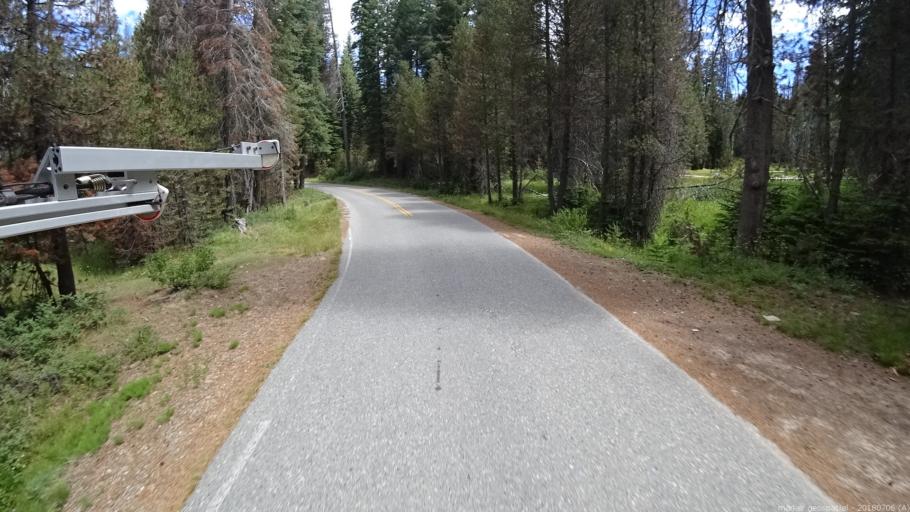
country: US
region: California
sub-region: Madera County
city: Oakhurst
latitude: 37.4315
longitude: -119.4306
